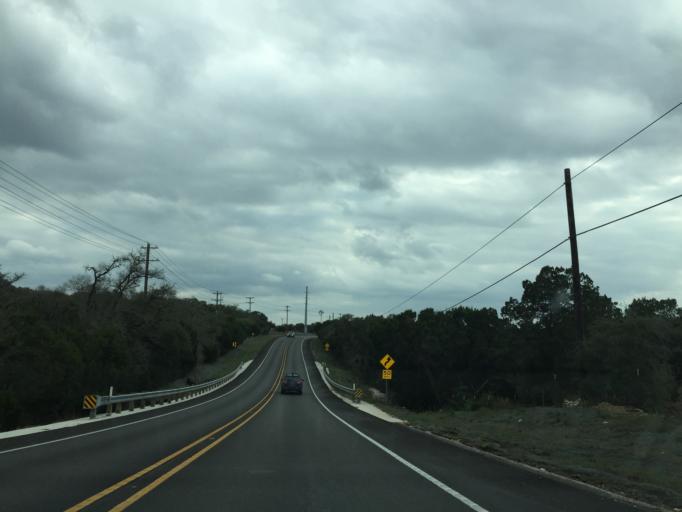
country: US
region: Texas
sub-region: Travis County
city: Shady Hollow
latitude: 30.1780
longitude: -97.9288
